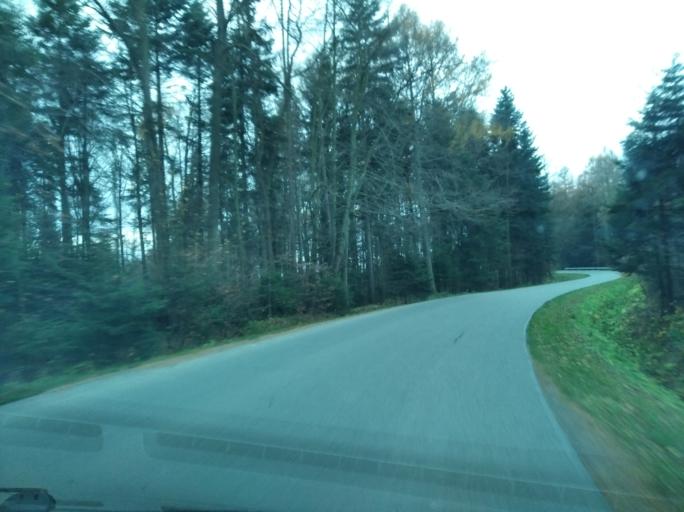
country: PL
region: Subcarpathian Voivodeship
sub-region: Powiat ropczycko-sedziszowski
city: Zagorzyce
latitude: 49.9608
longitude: 21.6928
